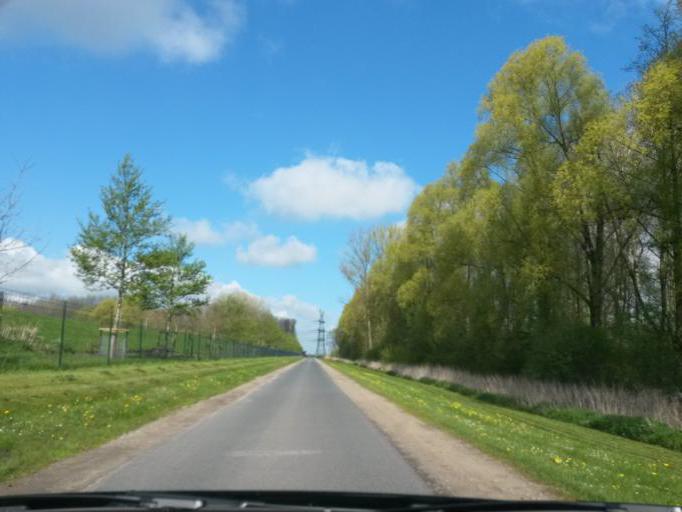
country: DE
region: Schleswig-Holstein
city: Hetlingen
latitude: 53.6048
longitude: 9.6224
